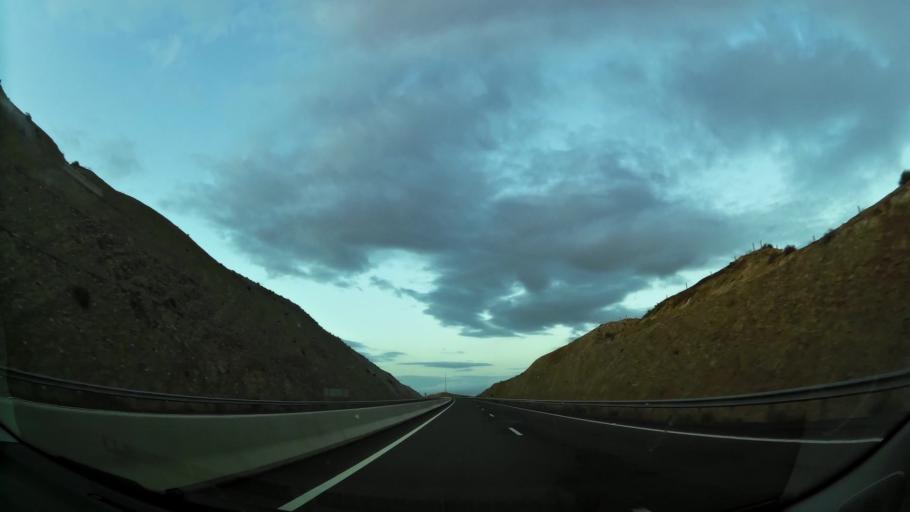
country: MA
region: Oriental
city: El Aioun
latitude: 34.5943
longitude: -2.6631
